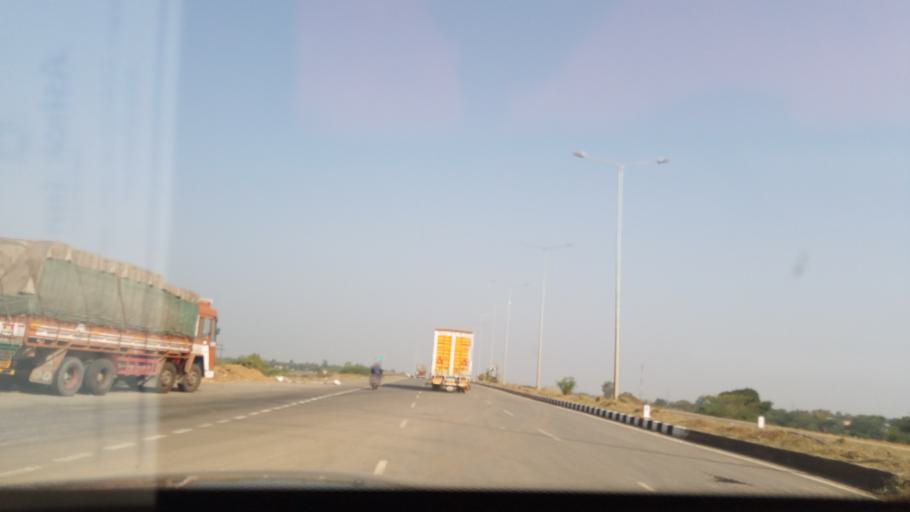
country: IN
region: Karnataka
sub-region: Haveri
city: Haveri
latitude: 14.8596
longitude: 75.3231
